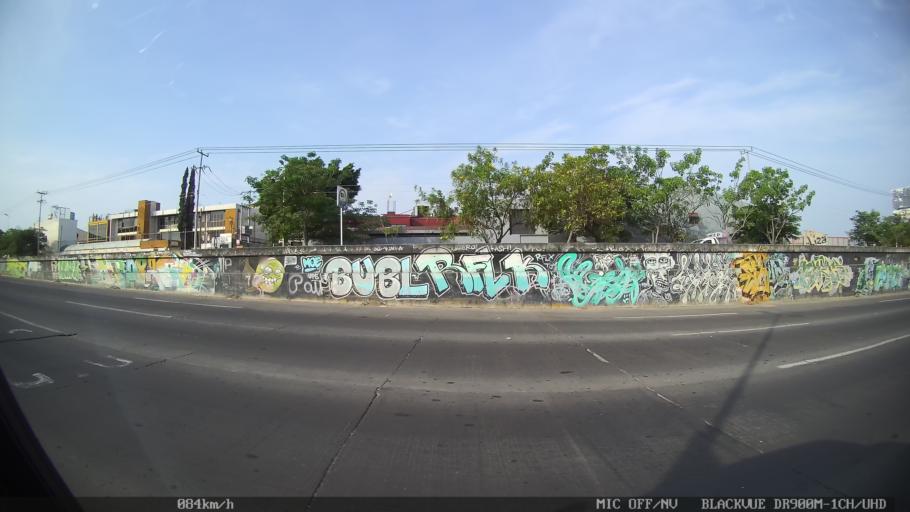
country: MX
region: Jalisco
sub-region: Zapopan
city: Zapopan
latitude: 20.7200
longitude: -103.3143
